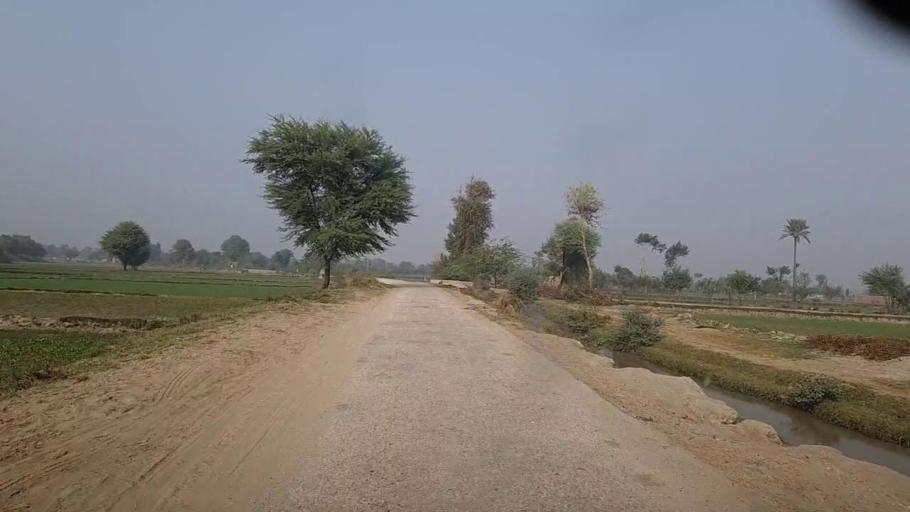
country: PK
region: Sindh
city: Bozdar
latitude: 27.0667
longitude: 68.6373
